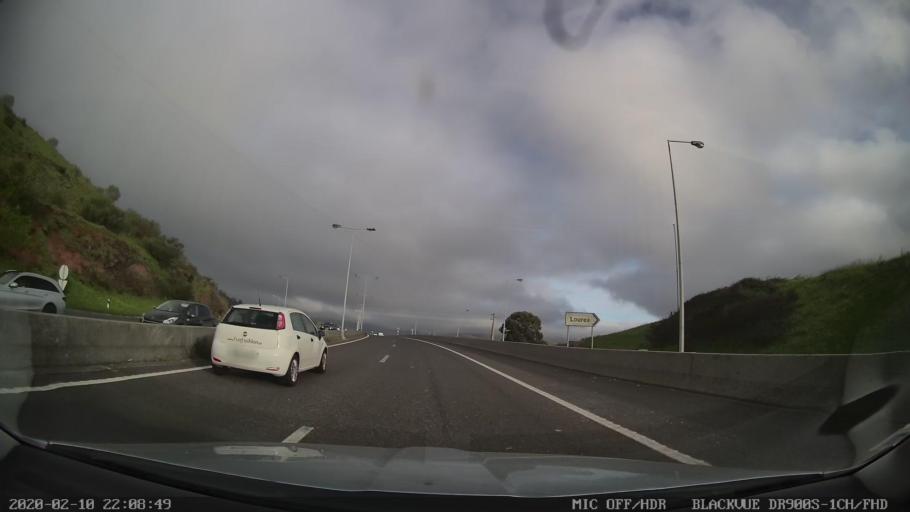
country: PT
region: Lisbon
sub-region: Odivelas
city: Ramada
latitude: 38.8134
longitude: -9.1833
